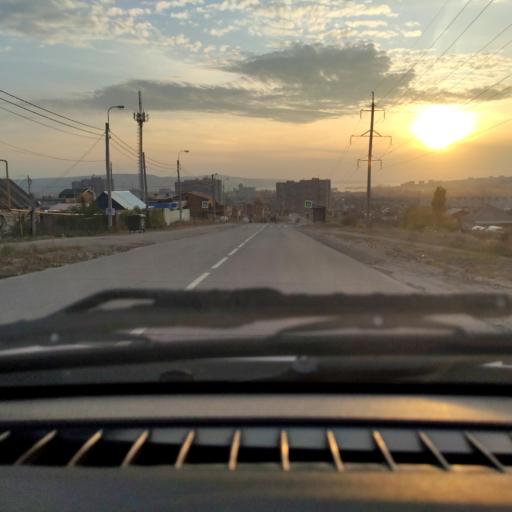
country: RU
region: Samara
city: Zhigulevsk
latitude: 53.4852
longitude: 49.5334
